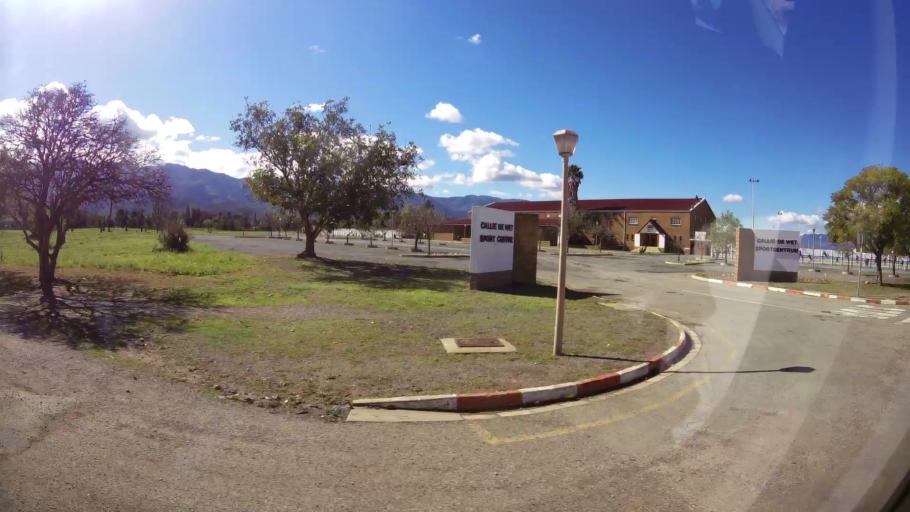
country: ZA
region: Western Cape
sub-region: Cape Winelands District Municipality
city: Ashton
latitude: -33.8130
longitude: 19.8925
